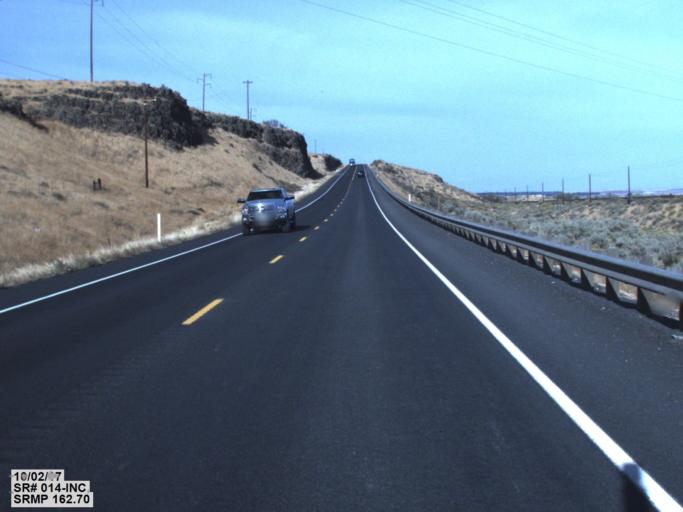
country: US
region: Oregon
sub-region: Morrow County
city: Boardman
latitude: 45.9015
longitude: -119.6819
